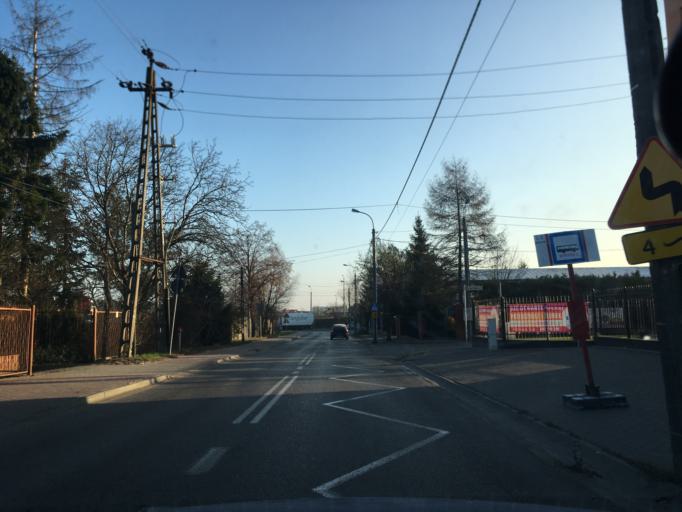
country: PL
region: Masovian Voivodeship
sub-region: Powiat piaseczynski
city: Piaseczno
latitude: 52.0713
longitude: 21.0097
